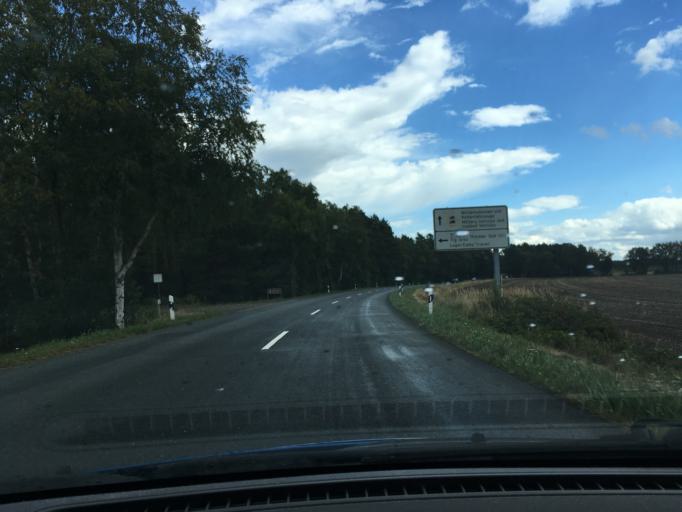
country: DE
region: Lower Saxony
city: Wietzendorf
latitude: 52.9345
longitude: 9.9961
